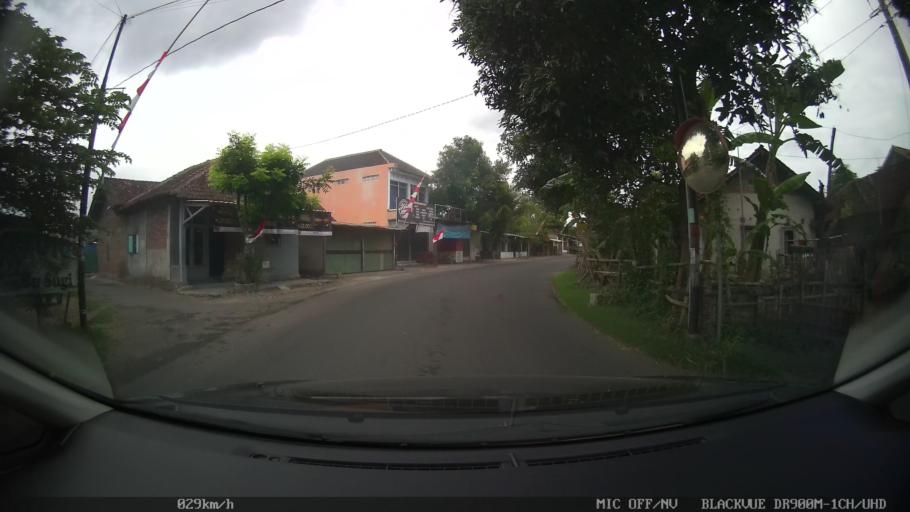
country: ID
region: Daerah Istimewa Yogyakarta
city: Sewon
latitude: -7.8732
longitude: 110.4073
